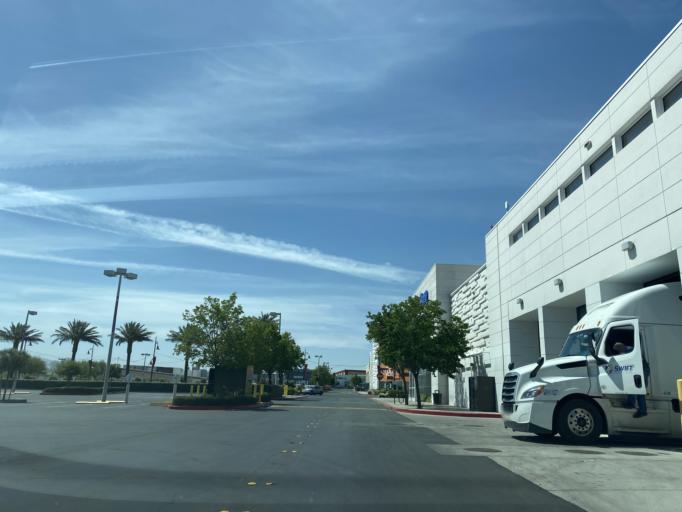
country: US
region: Nevada
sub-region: Clark County
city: Paradise
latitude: 36.0690
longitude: -115.1740
